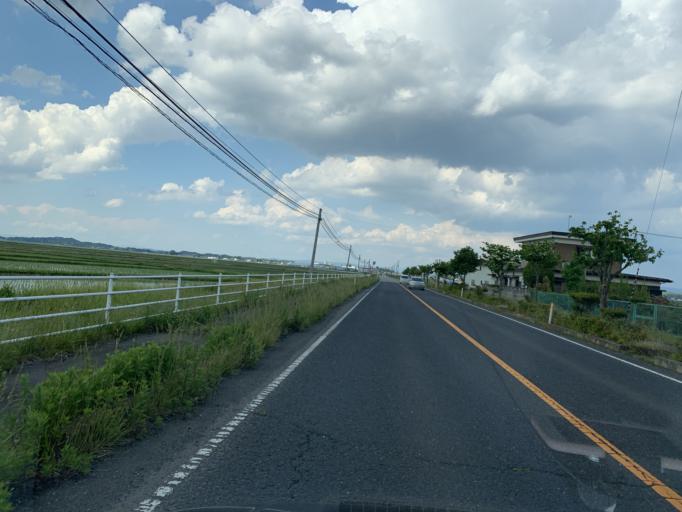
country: JP
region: Miyagi
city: Wakuya
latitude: 38.6192
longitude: 141.1812
